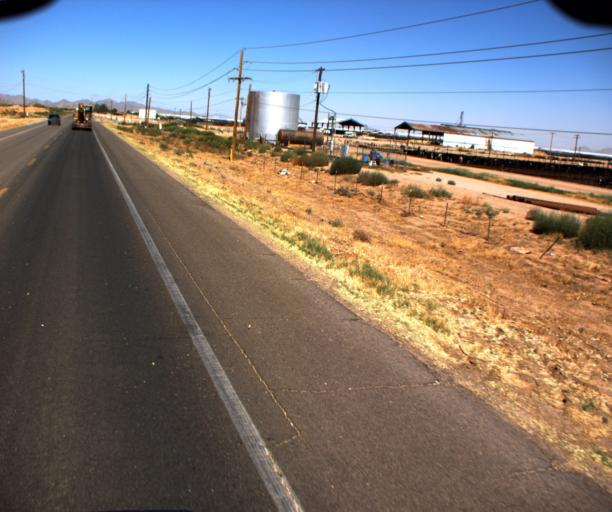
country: US
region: Arizona
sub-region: Pinal County
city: Maricopa
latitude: 32.8794
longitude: -112.0131
